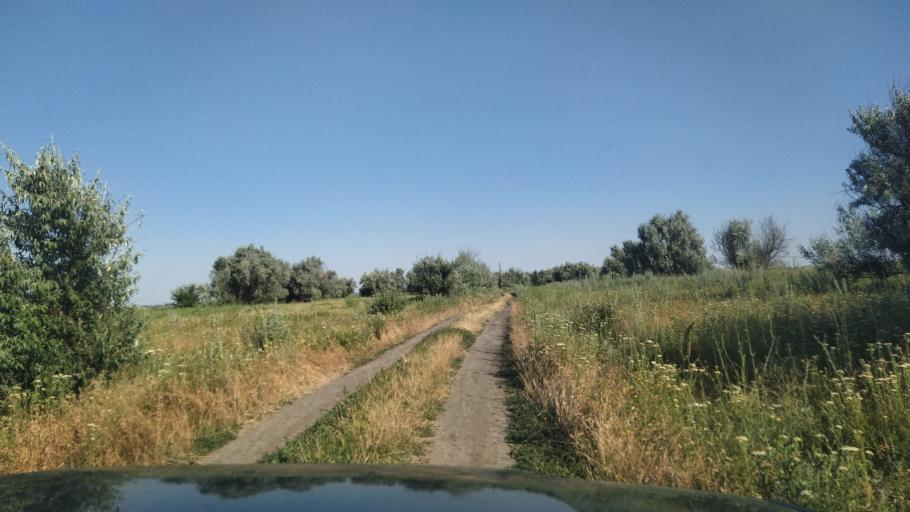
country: RU
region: Rostov
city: Kuleshovka
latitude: 47.1360
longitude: 39.6401
